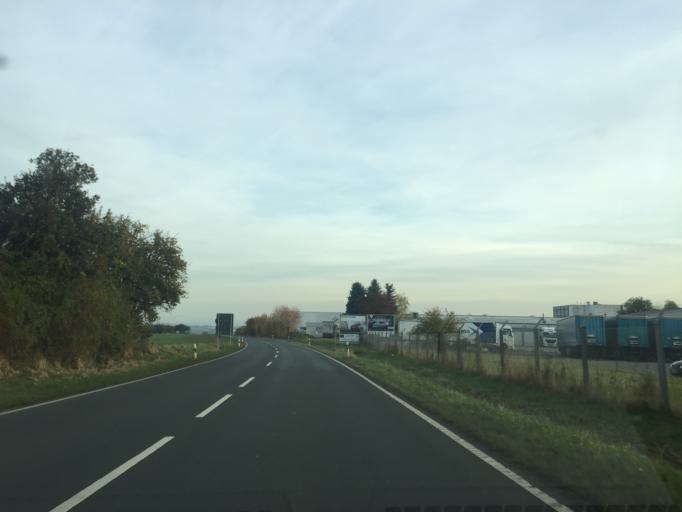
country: DE
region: Hesse
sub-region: Regierungsbezirk Giessen
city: Elz
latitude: 50.4247
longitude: 8.0194
